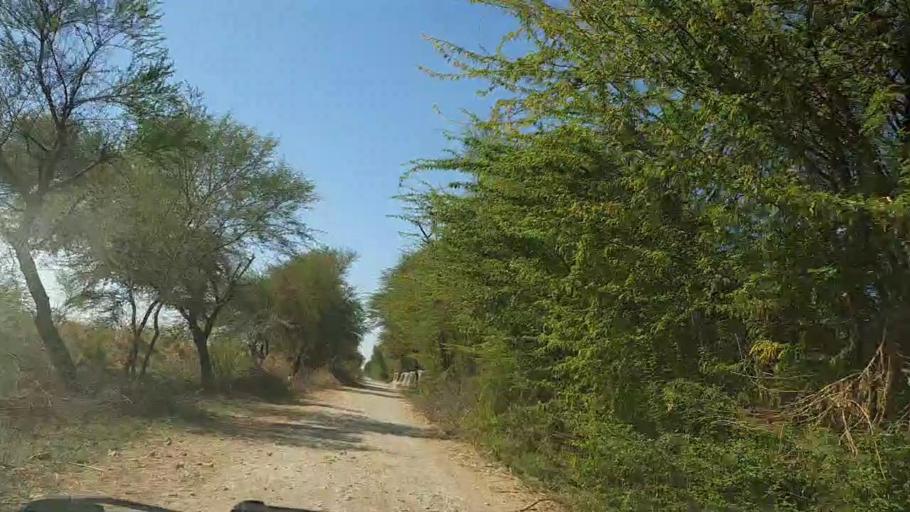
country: PK
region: Sindh
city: Dhoro Naro
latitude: 25.5220
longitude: 69.5138
